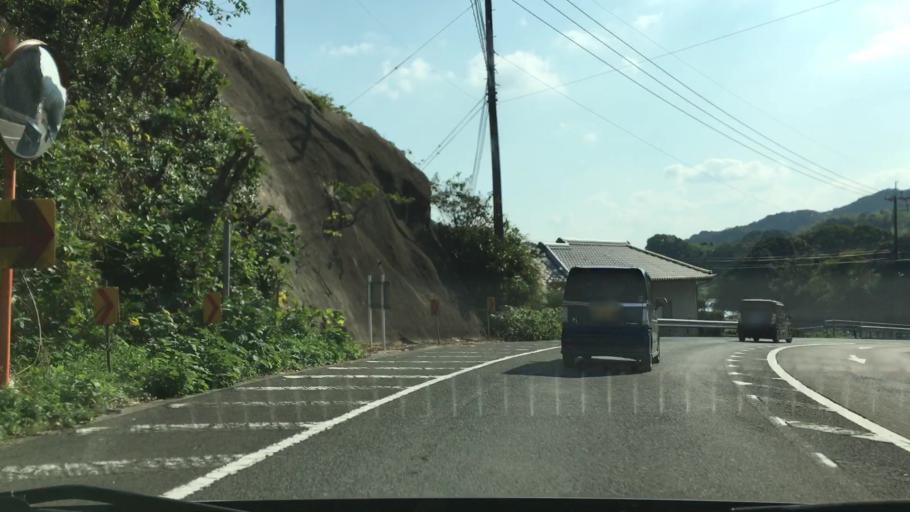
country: JP
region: Nagasaki
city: Togitsu
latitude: 32.9366
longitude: 129.7841
